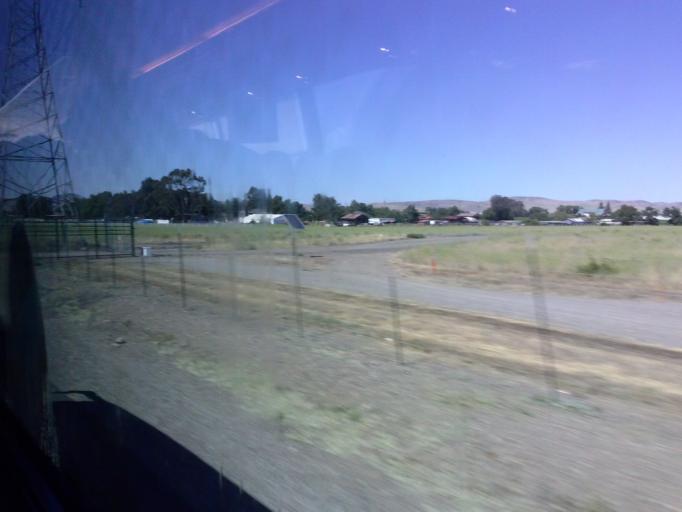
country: US
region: California
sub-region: Alameda County
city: Livermore
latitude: 37.6616
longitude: -121.7329
